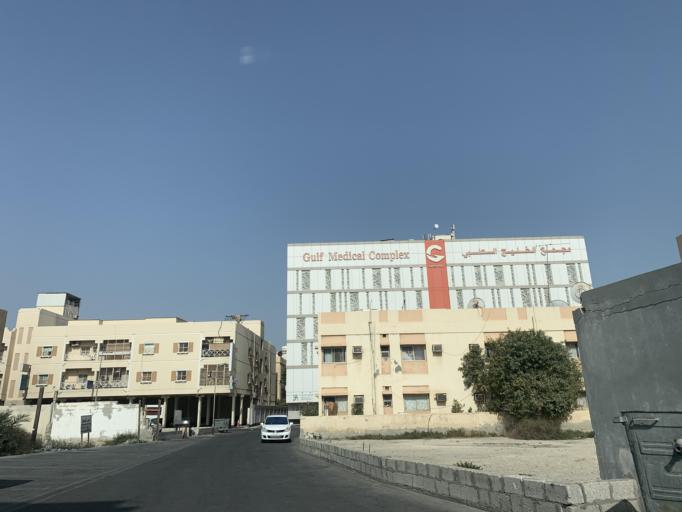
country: BH
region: Manama
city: Manama
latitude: 26.2160
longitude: 50.5676
